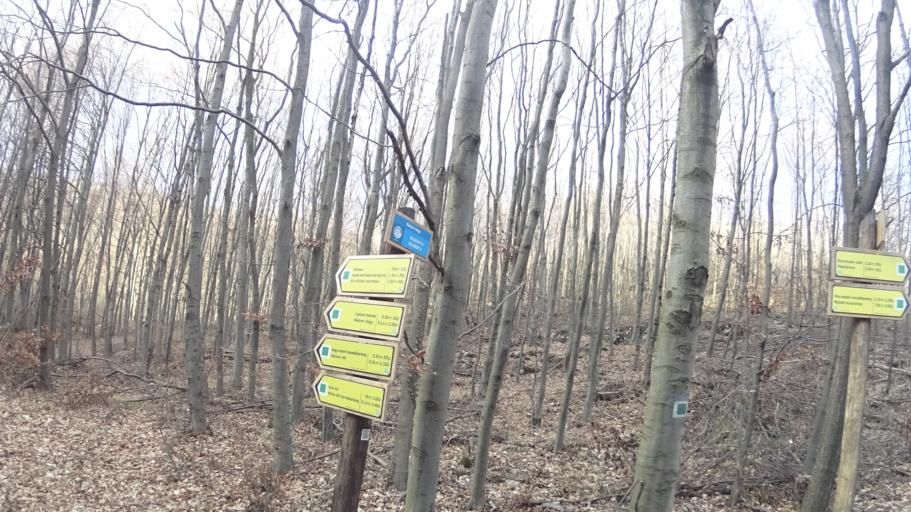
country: HU
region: Heves
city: Szilvasvarad
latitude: 48.0618
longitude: 20.5009
